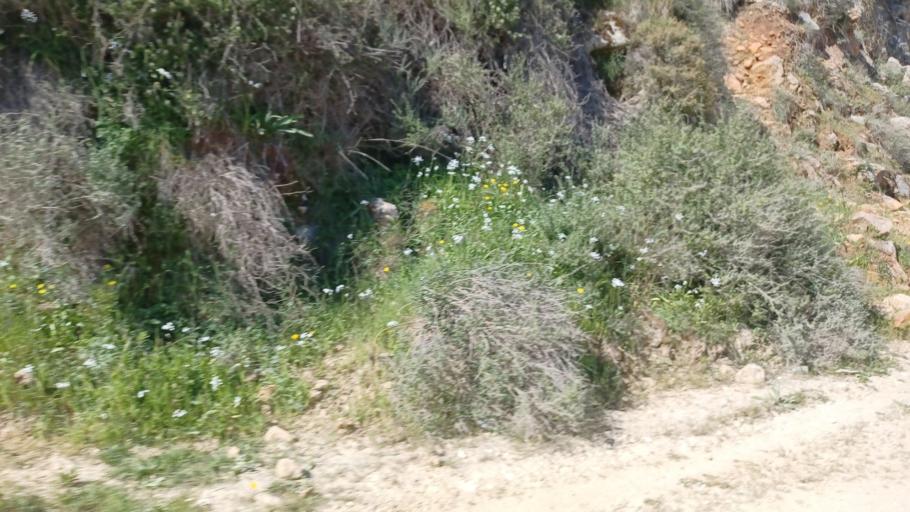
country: CY
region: Pafos
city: Polis
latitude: 35.0012
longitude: 32.3955
